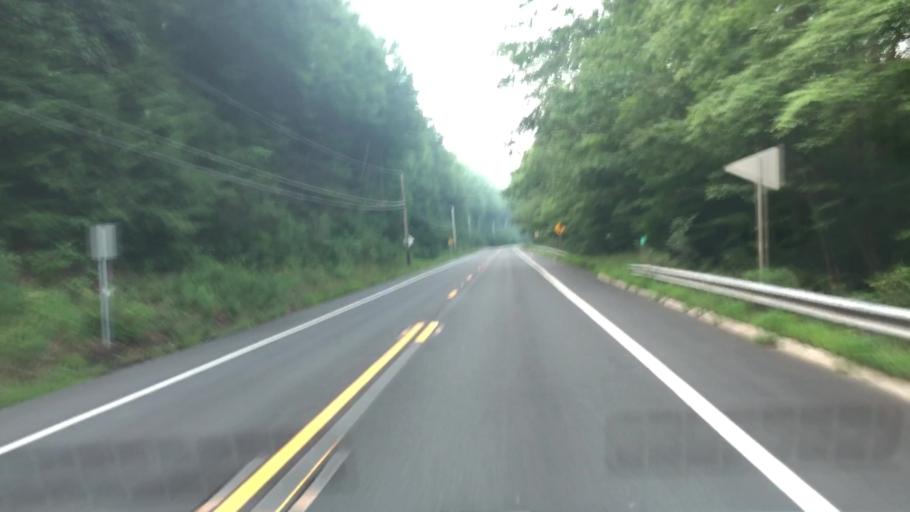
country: US
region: Massachusetts
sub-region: Franklin County
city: Ashfield
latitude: 42.5493
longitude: -72.8019
